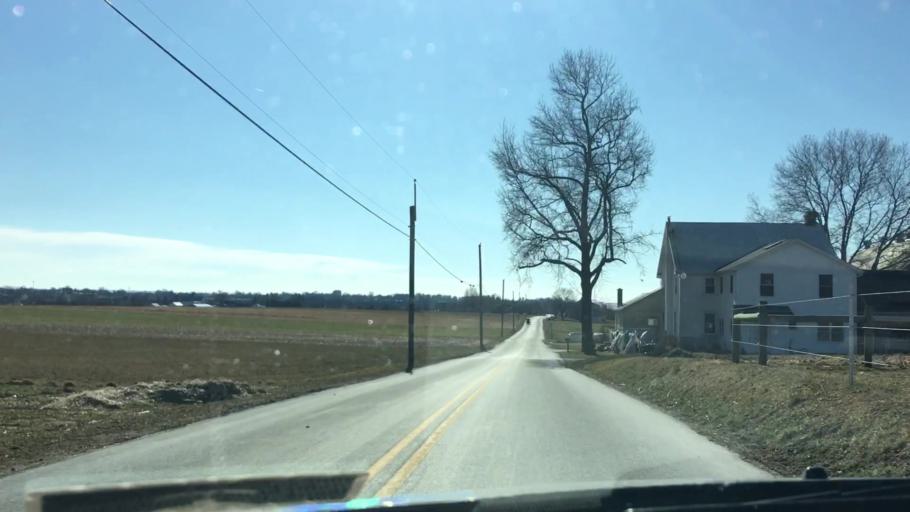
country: US
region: Pennsylvania
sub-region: Lancaster County
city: Brownstown
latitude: 40.0664
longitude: -76.2306
